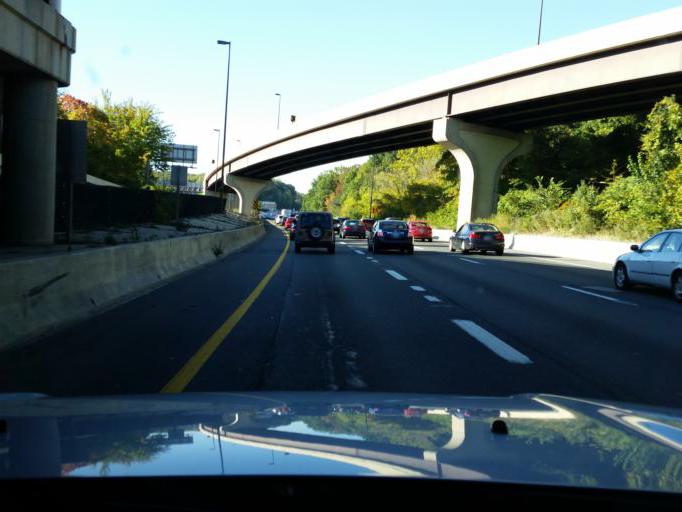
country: US
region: Maryland
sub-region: Montgomery County
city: North Bethesda
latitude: 39.0334
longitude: -77.1424
